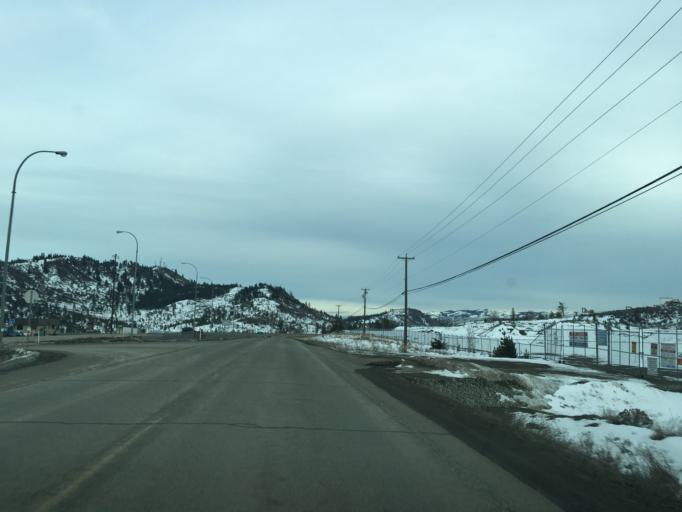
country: CA
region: British Columbia
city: Kamloops
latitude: 50.6649
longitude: -120.4247
